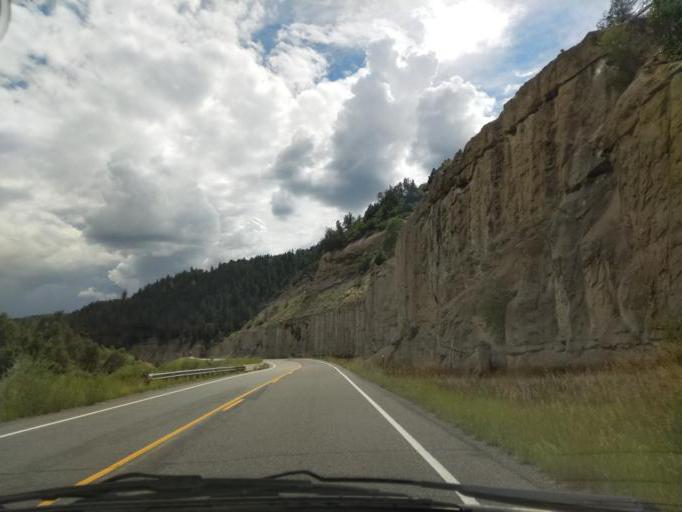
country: US
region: Colorado
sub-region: Delta County
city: Paonia
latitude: 39.0120
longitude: -107.3614
